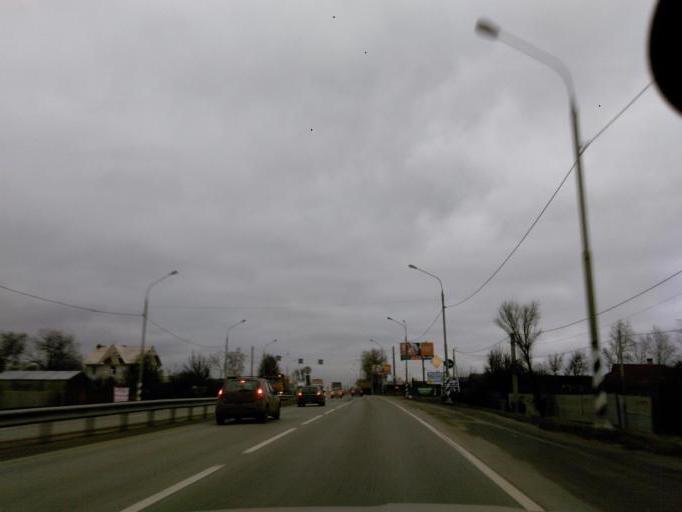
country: RU
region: Moskovskaya
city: Chashnikovo
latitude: 56.0485
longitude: 37.1553
